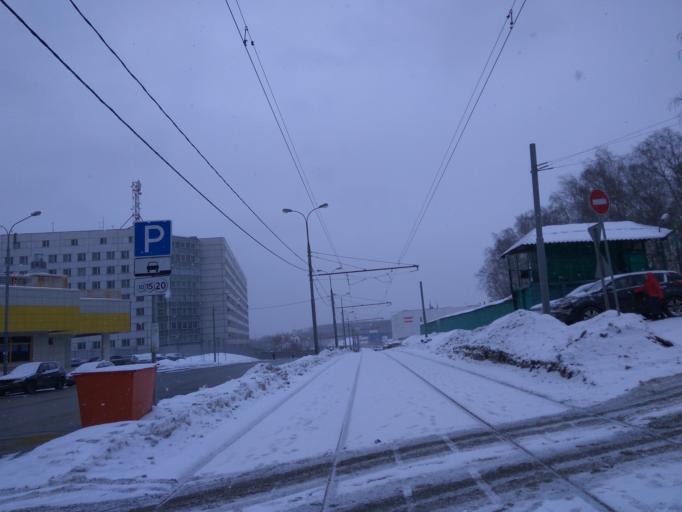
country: RU
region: Moscow
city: Strogino
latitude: 55.7991
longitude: 37.3885
